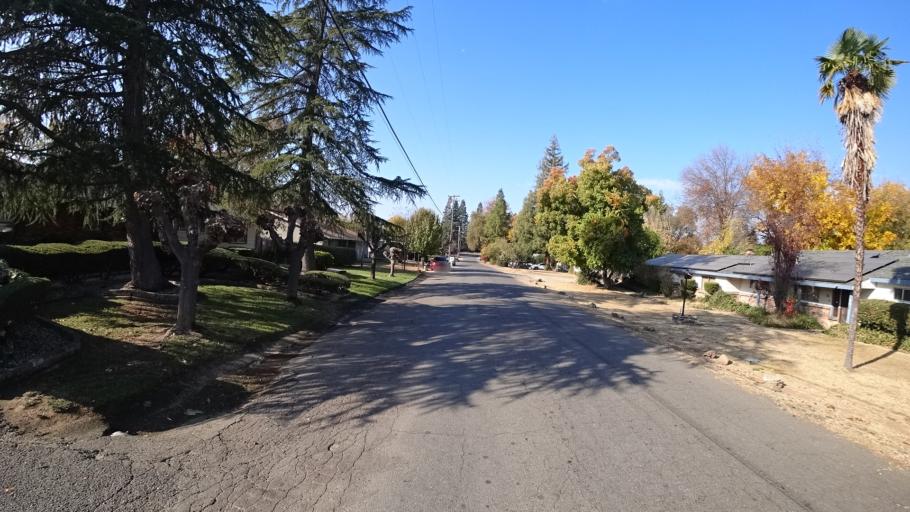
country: US
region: California
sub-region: Sacramento County
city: Citrus Heights
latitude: 38.7134
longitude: -121.2697
